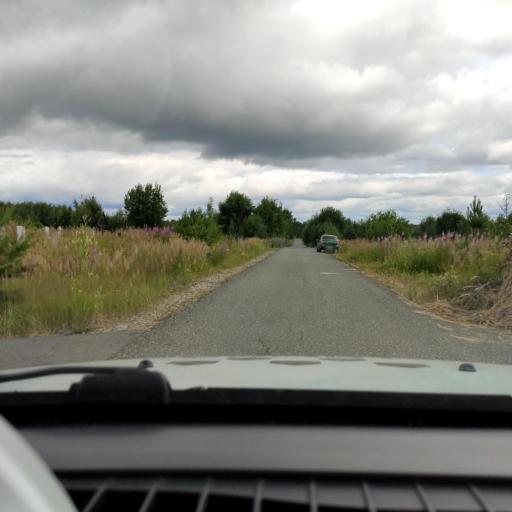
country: RU
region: Perm
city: Kondratovo
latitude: 58.0641
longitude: 56.1529
